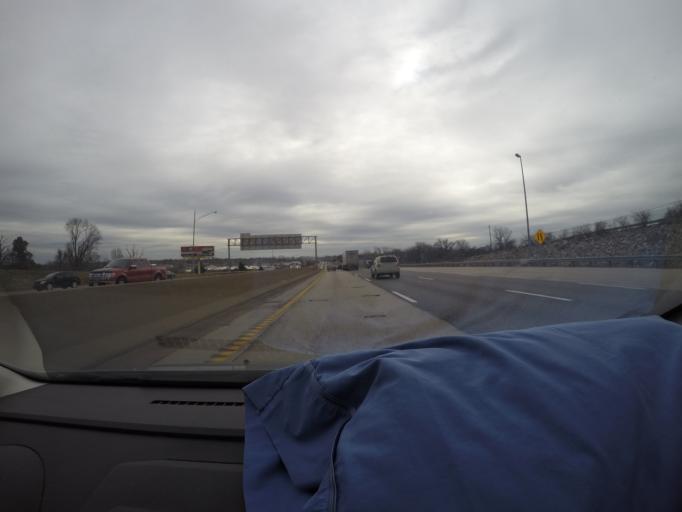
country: US
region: Missouri
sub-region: Saint Louis County
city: Bridgeton
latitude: 38.7461
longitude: -90.4328
